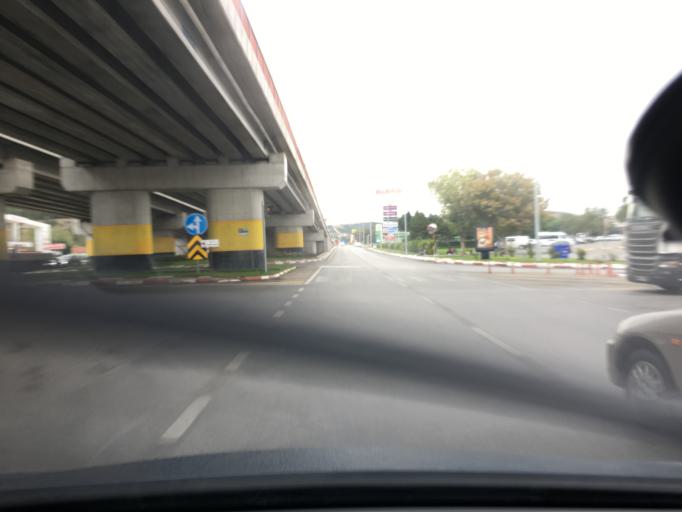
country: TR
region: Afyonkarahisar
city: Afyonkarahisar
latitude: 38.7906
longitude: 30.4561
